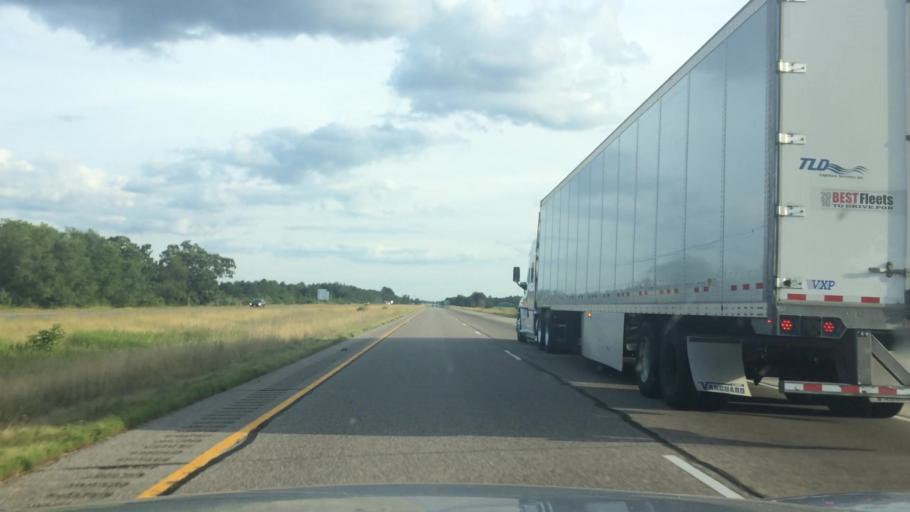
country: US
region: Wisconsin
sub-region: Portage County
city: Plover
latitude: 44.2435
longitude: -89.5243
